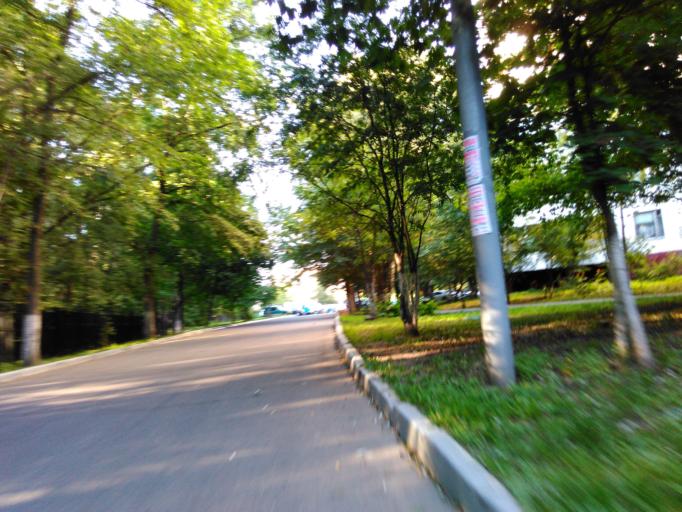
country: RU
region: Moscow
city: Tyoply Stan
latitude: 55.6342
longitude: 37.5083
